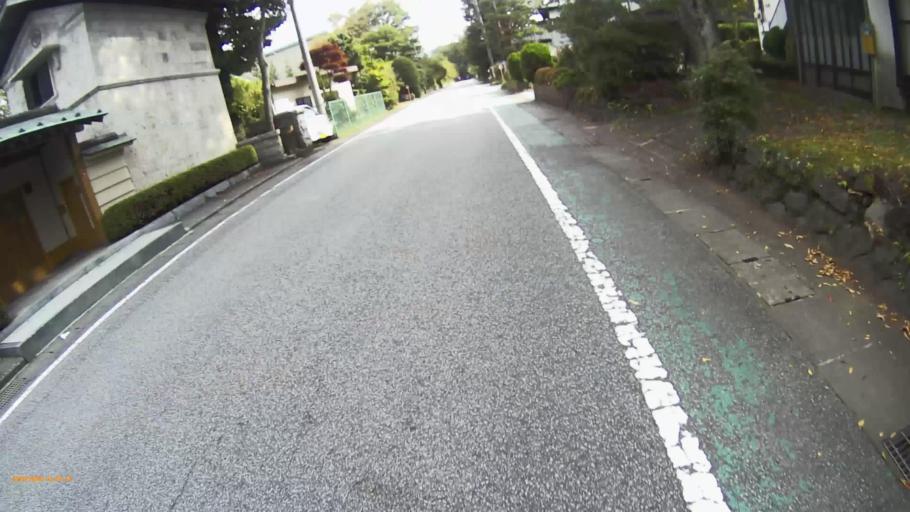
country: JP
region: Shizuoka
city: Gotemba
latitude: 35.4184
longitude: 138.8530
